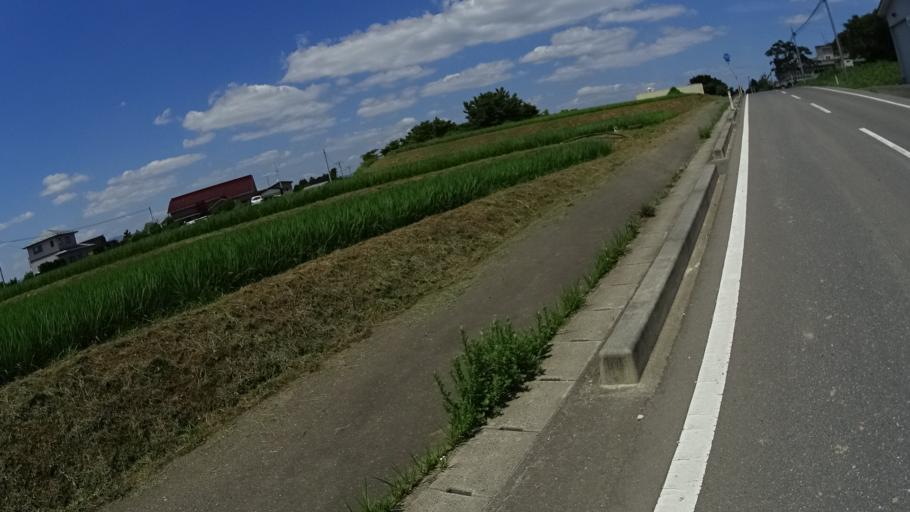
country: JP
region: Iwate
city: Ofunato
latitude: 38.8459
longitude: 141.6187
